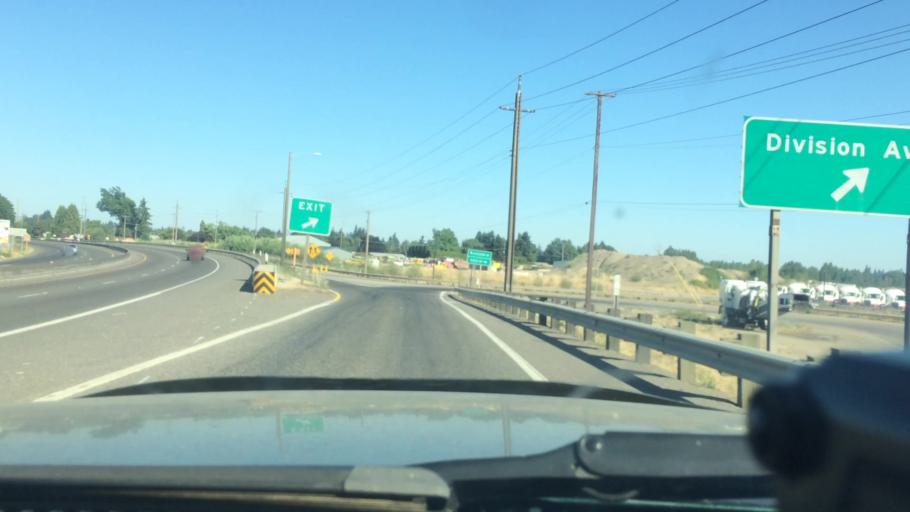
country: US
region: Oregon
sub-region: Lane County
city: Eugene
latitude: 44.0969
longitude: -123.1094
